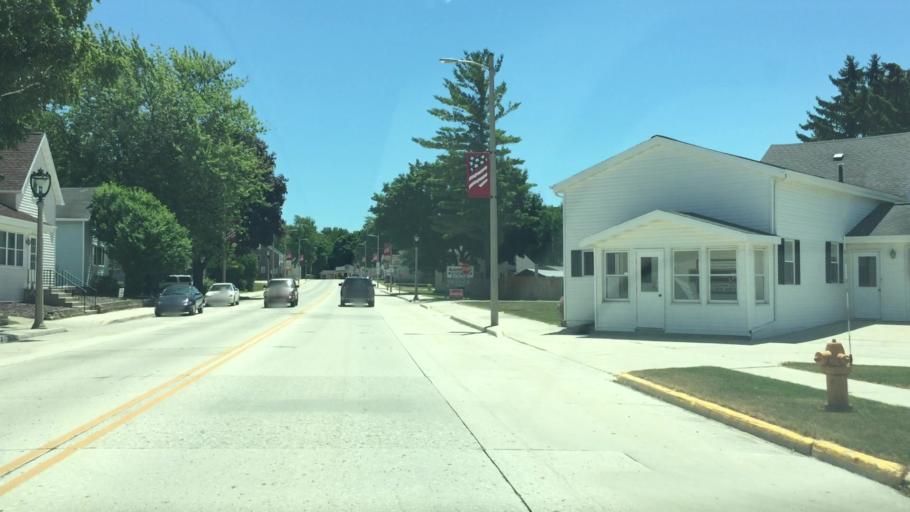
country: US
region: Wisconsin
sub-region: Calumet County
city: New Holstein
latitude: 43.9517
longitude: -88.1011
